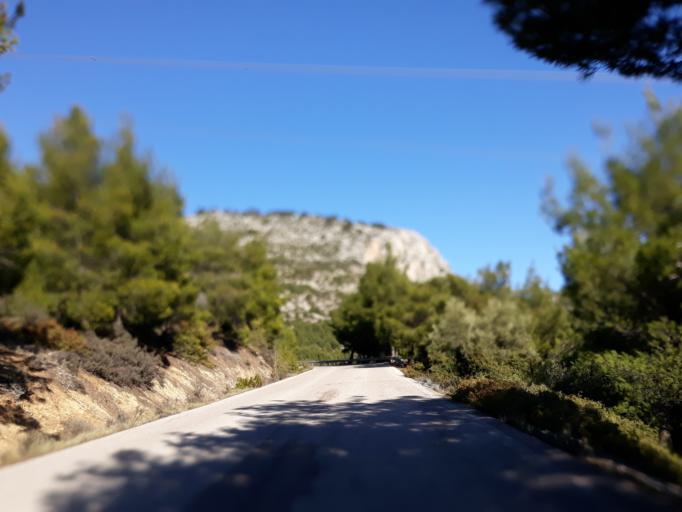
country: GR
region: Attica
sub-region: Nomarchia Dytikis Attikis
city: Fyli
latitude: 38.1304
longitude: 23.6484
